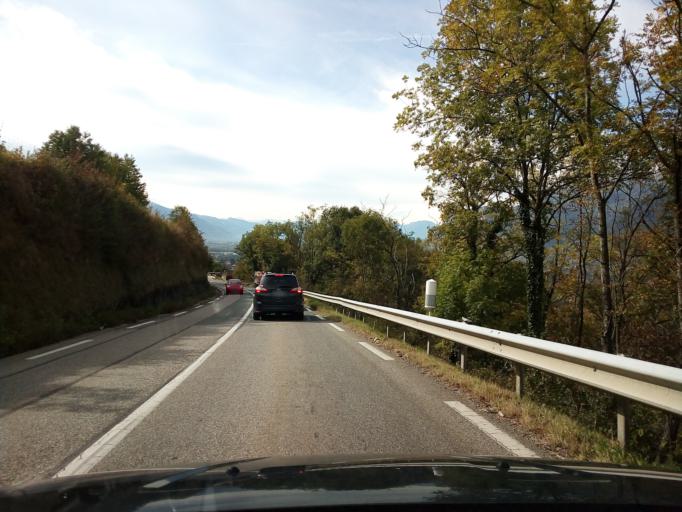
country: FR
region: Rhone-Alpes
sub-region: Departement de l'Isere
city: Le Cheylas
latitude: 45.3578
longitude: 5.9935
